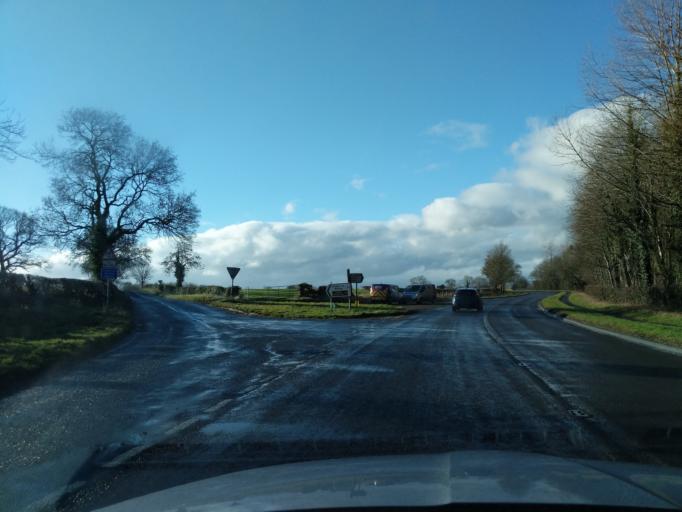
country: GB
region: England
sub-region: North Yorkshire
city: Bedale
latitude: 54.2955
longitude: -1.6110
